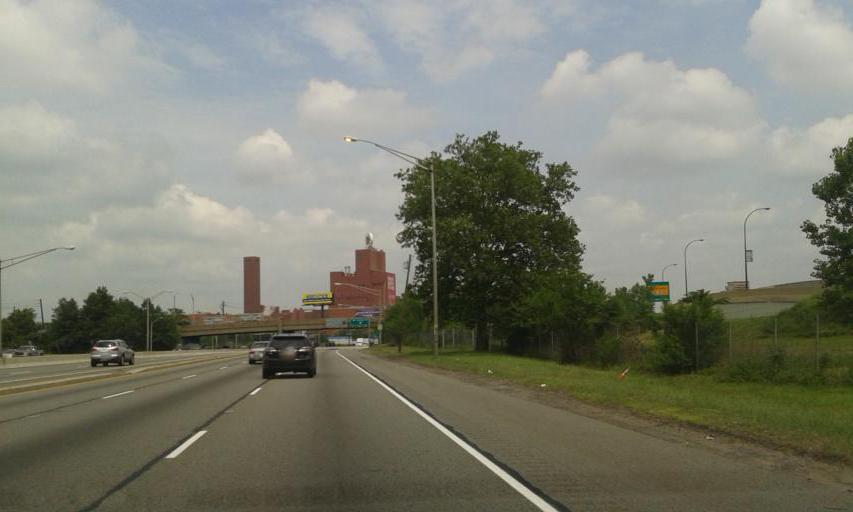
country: US
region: New Jersey
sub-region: Union County
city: Elizabeth
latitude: 40.6863
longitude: -74.1925
